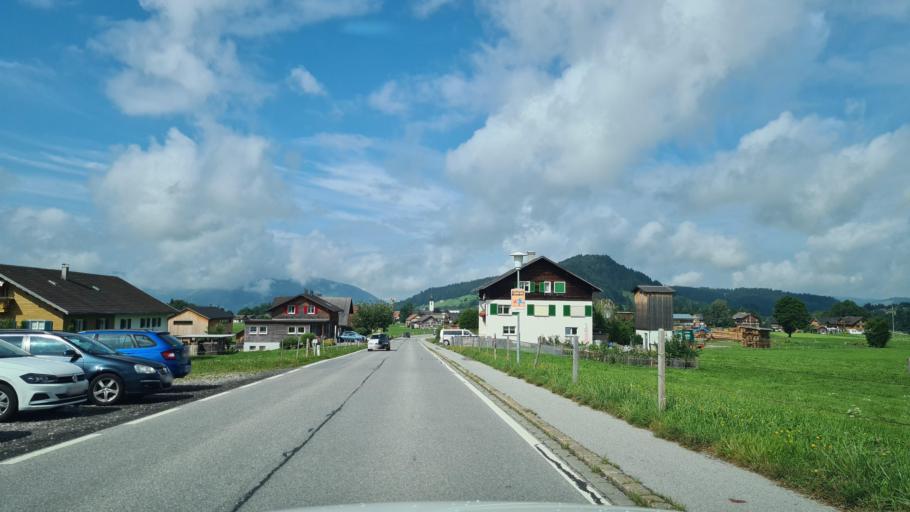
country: AT
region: Vorarlberg
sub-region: Politischer Bezirk Bregenz
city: Riefensberg
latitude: 47.4569
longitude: 9.9772
